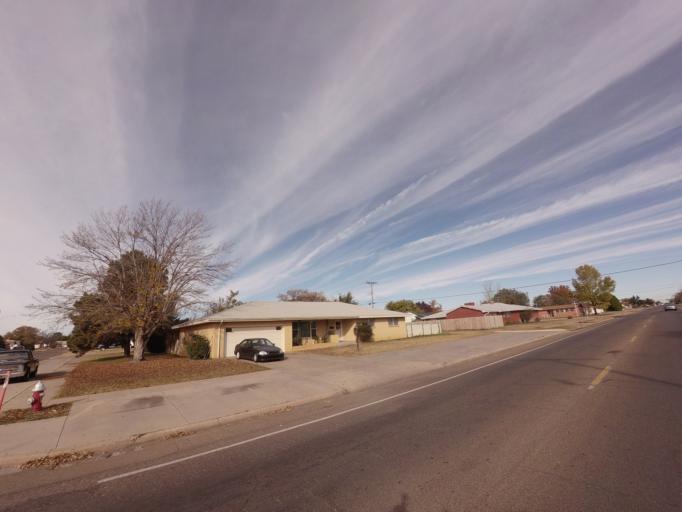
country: US
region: New Mexico
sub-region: Curry County
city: Clovis
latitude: 34.4223
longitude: -103.2142
